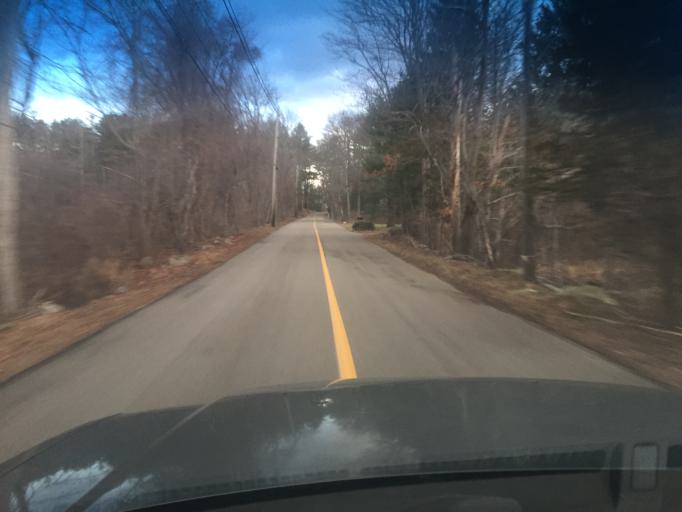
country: US
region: Massachusetts
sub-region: Norfolk County
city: Medway
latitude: 42.1556
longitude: -71.4340
